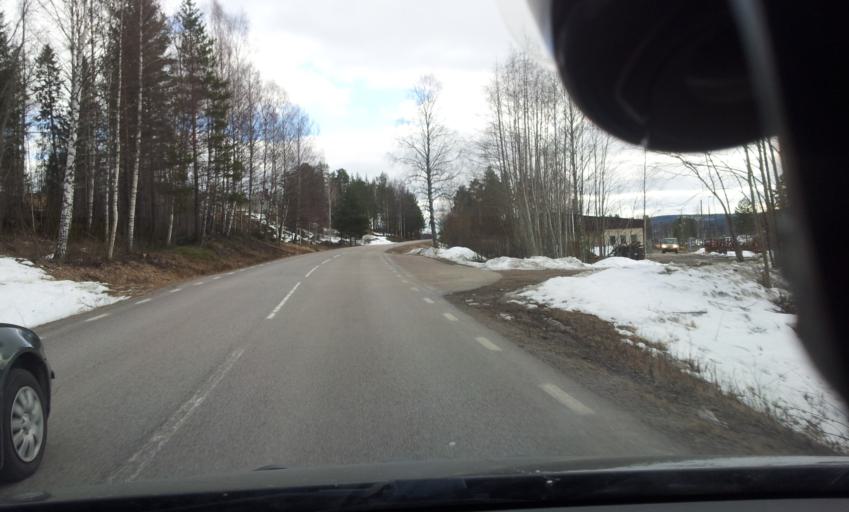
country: SE
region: Vaesternorrland
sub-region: Ange Kommun
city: Ange
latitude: 62.1599
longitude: 15.6770
